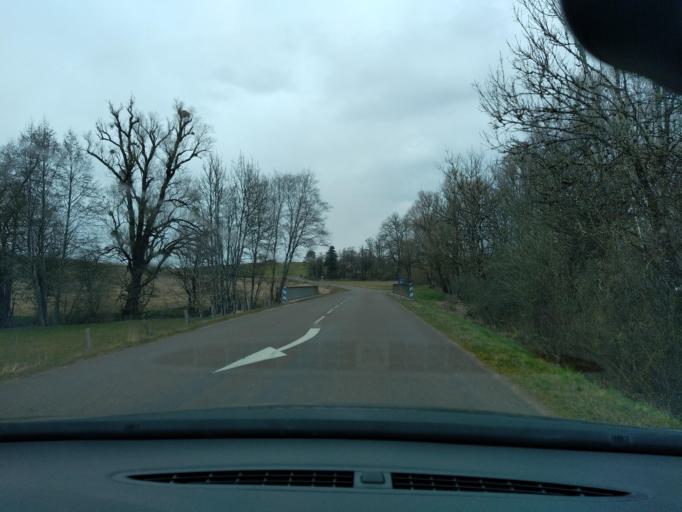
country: FR
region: Franche-Comte
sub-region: Departement du Jura
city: Arinthod
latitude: 46.4374
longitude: 5.5598
